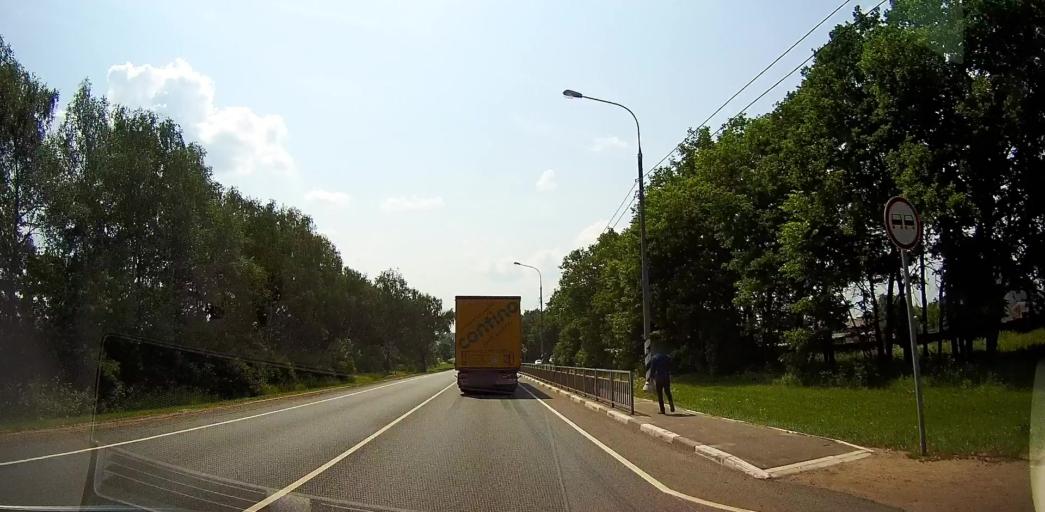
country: RU
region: Moskovskaya
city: Meshcherino
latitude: 55.1951
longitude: 38.3668
